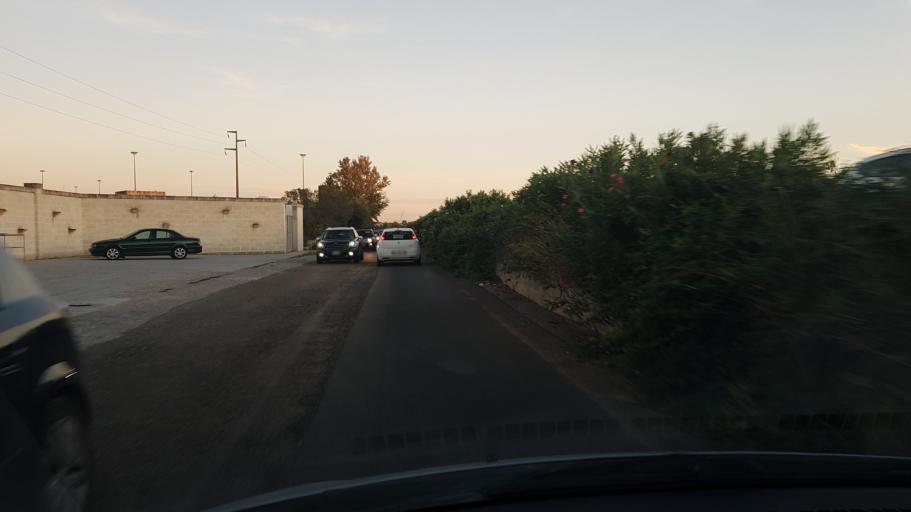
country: IT
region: Apulia
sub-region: Provincia di Lecce
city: Cavallino
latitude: 40.2978
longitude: 18.1950
